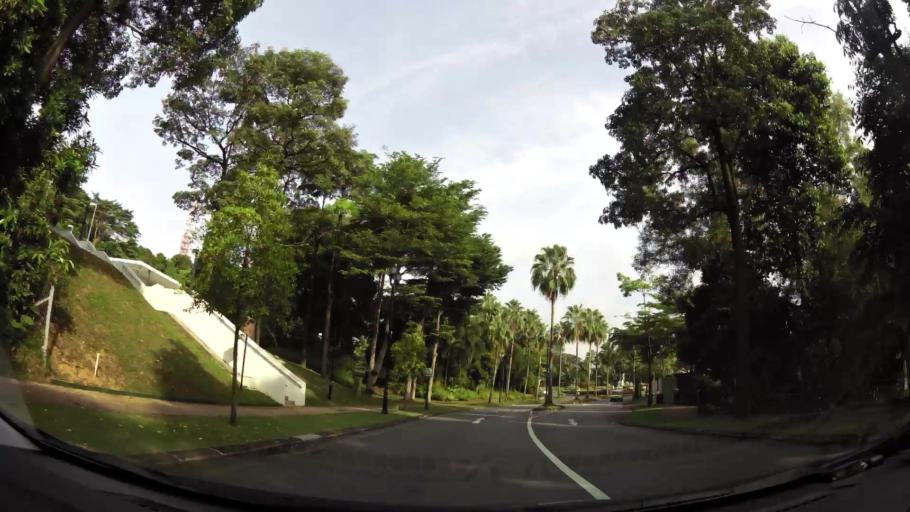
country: SG
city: Singapore
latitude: 1.2464
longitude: 103.8390
